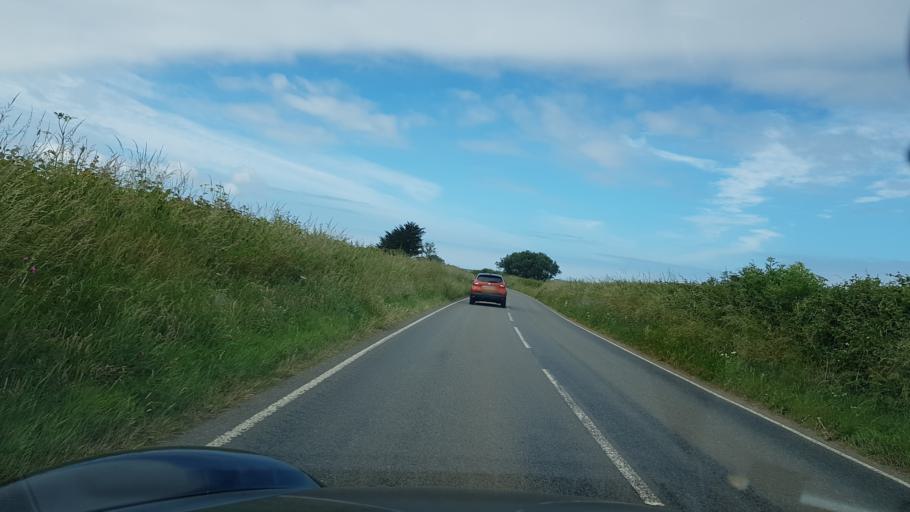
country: GB
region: Wales
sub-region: Pembrokeshire
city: Herbrandston
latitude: 51.7706
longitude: -5.0619
